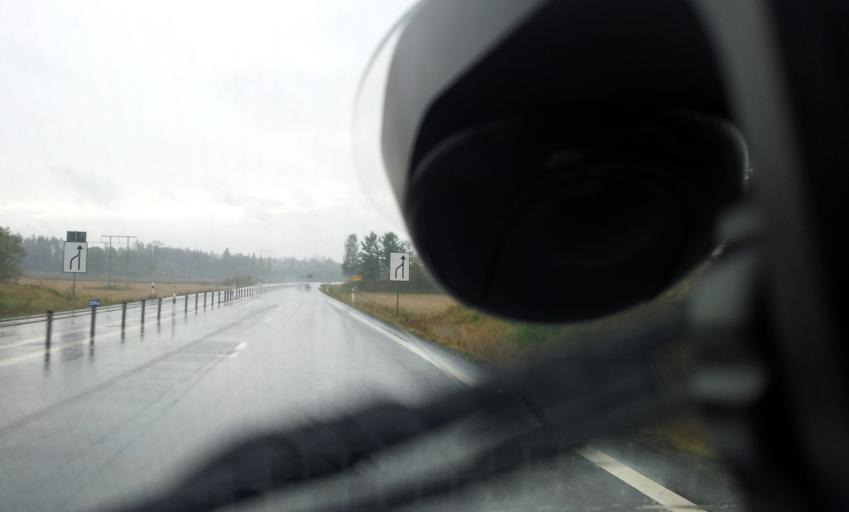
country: SE
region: OEstergoetland
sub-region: Valdemarsviks Kommun
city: Valdemarsvik
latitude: 58.0879
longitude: 16.5224
